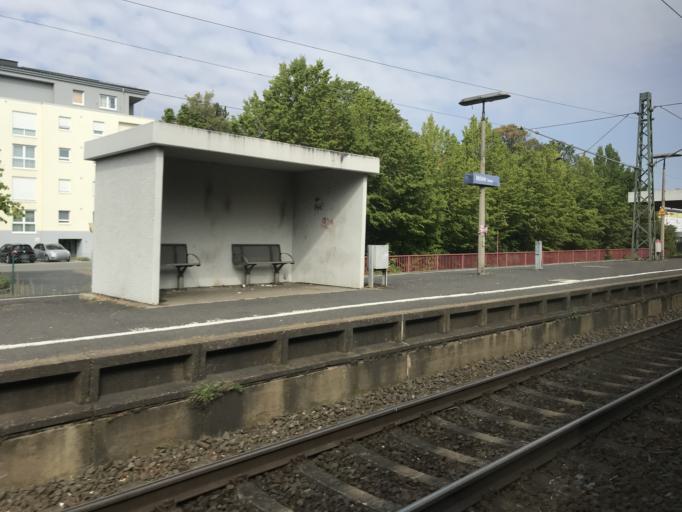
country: DE
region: Hesse
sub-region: Regierungsbezirk Darmstadt
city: Idstein
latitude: 50.2157
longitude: 8.2575
